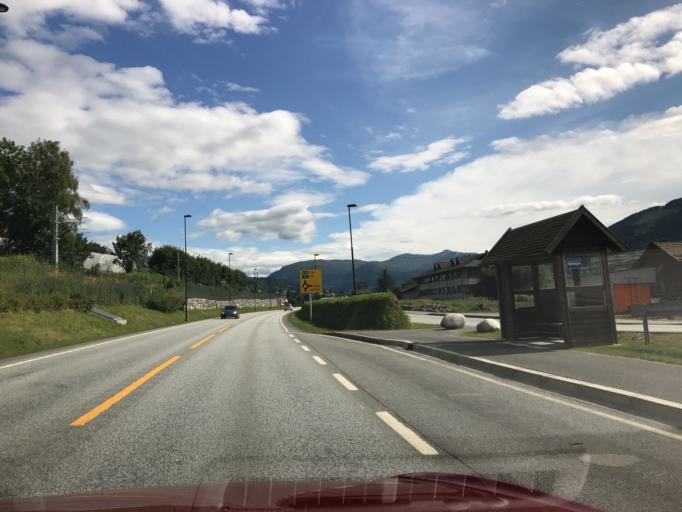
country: NO
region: Hordaland
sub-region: Voss
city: Voss
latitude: 60.6253
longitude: 6.3930
